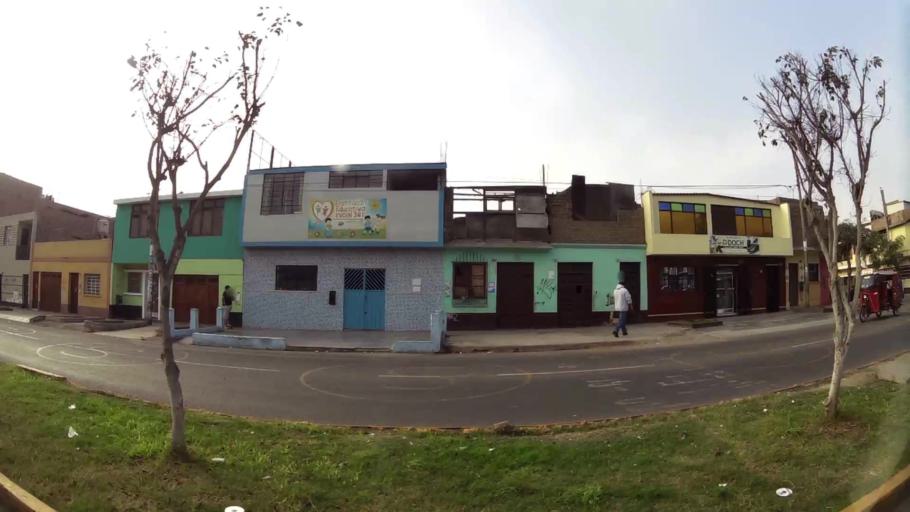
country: PE
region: Callao
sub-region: Callao
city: Callao
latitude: -12.0284
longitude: -77.0908
